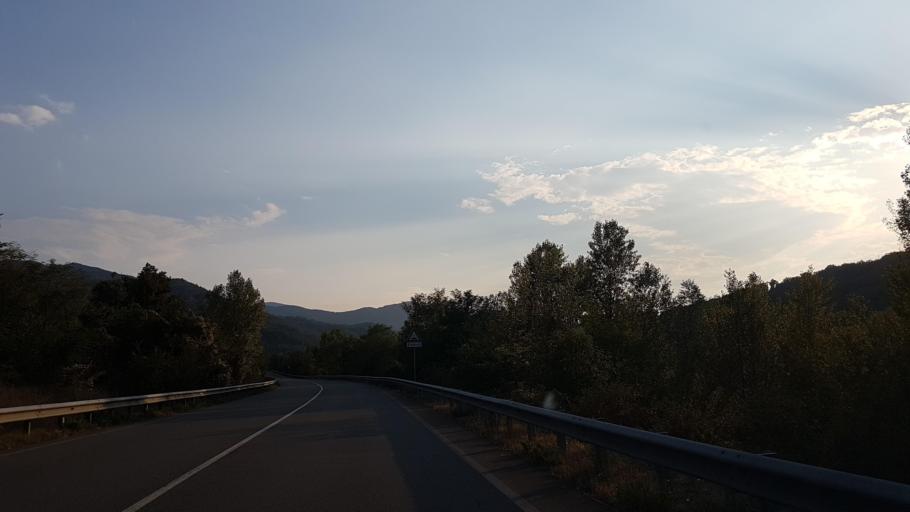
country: IT
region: Emilia-Romagna
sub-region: Provincia di Parma
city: Stazione Valmozzola
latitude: 44.5600
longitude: 9.9338
